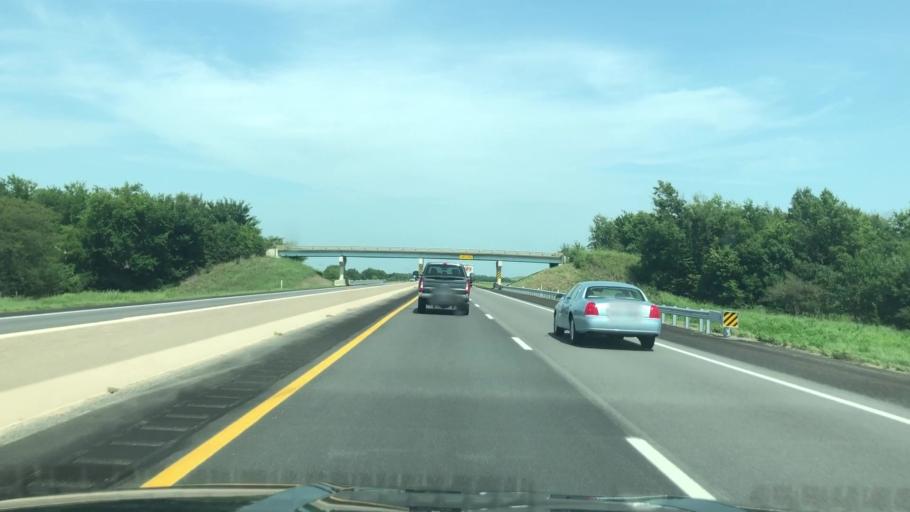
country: US
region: Oklahoma
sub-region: Craig County
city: Vinita
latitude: 36.6686
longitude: -95.0720
